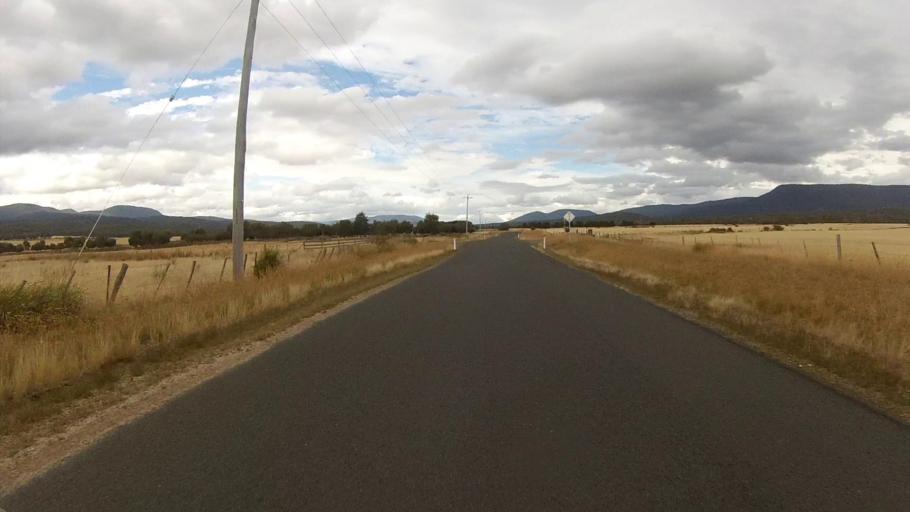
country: AU
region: Tasmania
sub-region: Break O'Day
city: St Helens
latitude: -41.8246
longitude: 147.8435
